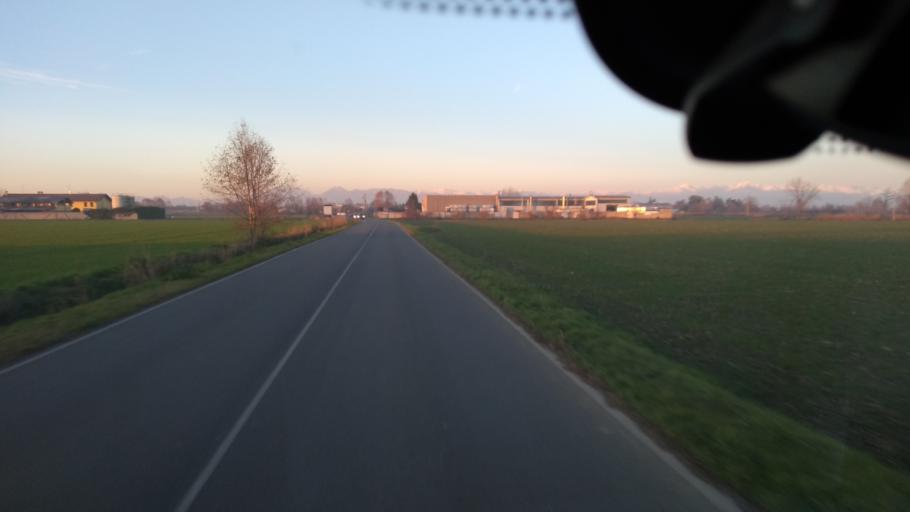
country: IT
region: Lombardy
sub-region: Provincia di Bergamo
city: Calvenzano
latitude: 45.4808
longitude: 9.6022
